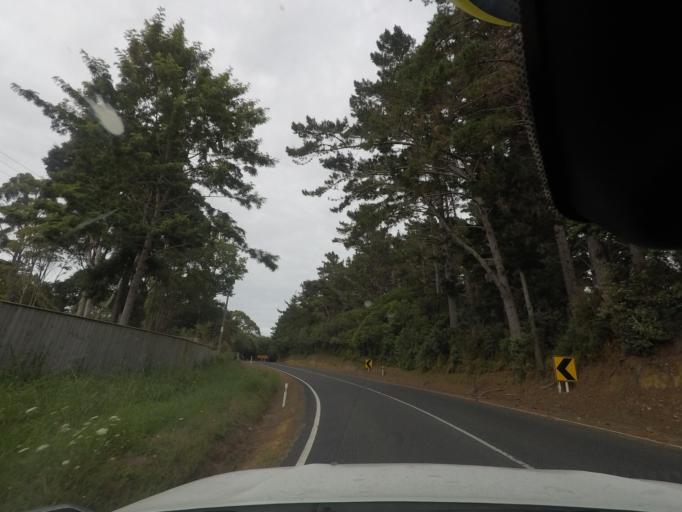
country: NZ
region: Auckland
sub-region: Auckland
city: Parakai
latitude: -36.5211
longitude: 174.2762
